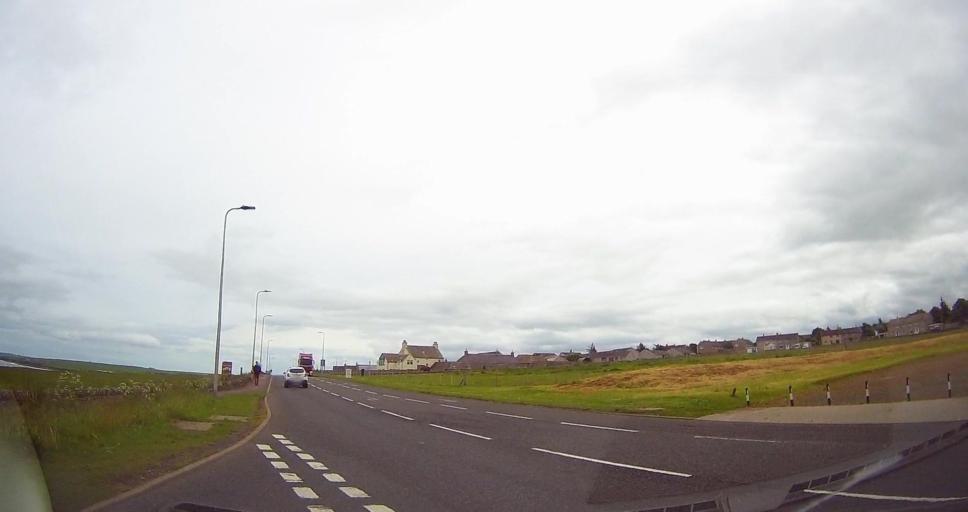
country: GB
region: Scotland
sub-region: Highland
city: Thurso
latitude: 58.5985
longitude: -3.5371
